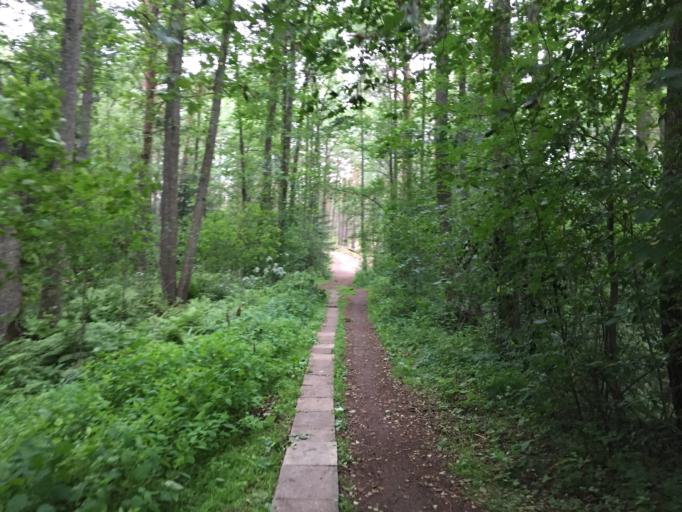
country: LV
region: Carnikava
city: Carnikava
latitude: 57.1197
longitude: 24.2215
